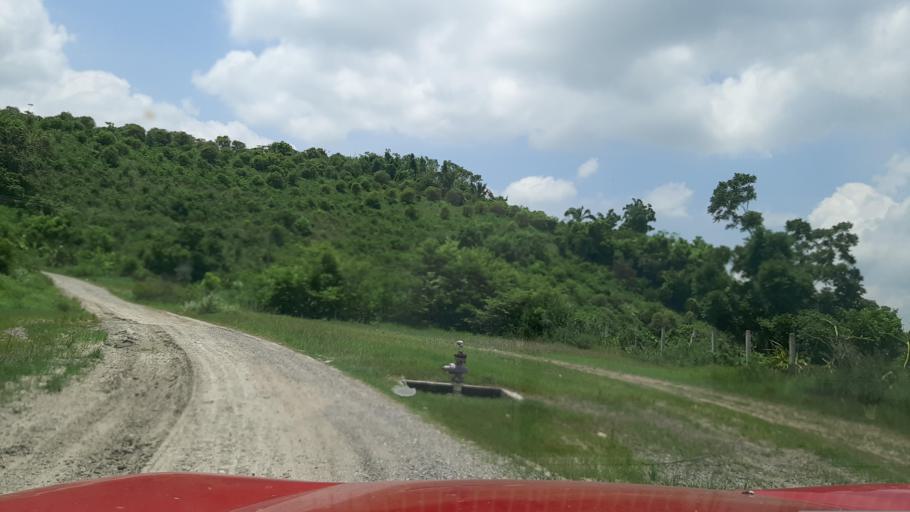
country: MX
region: Veracruz
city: Papantla de Olarte
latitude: 20.4246
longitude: -97.2676
